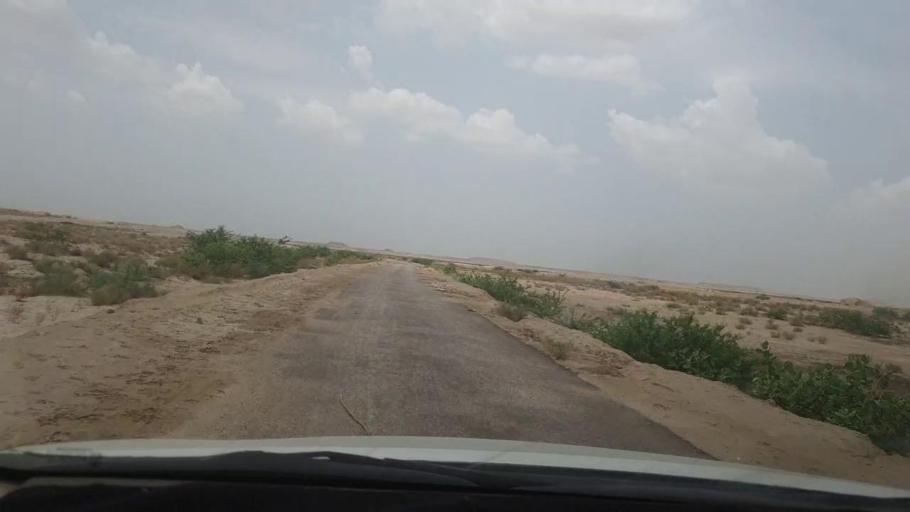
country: PK
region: Sindh
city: Khairpur
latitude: 27.3990
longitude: 68.9721
